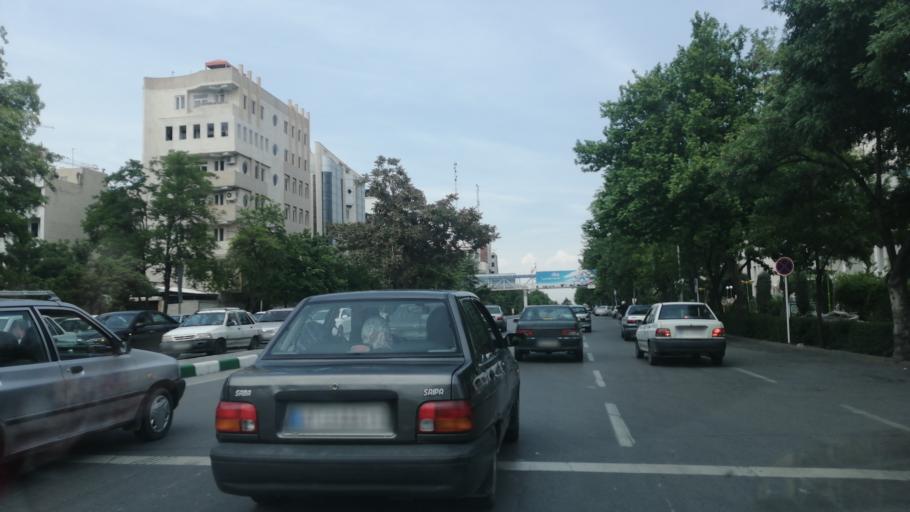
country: IR
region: Razavi Khorasan
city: Mashhad
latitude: 36.3196
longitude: 59.5653
